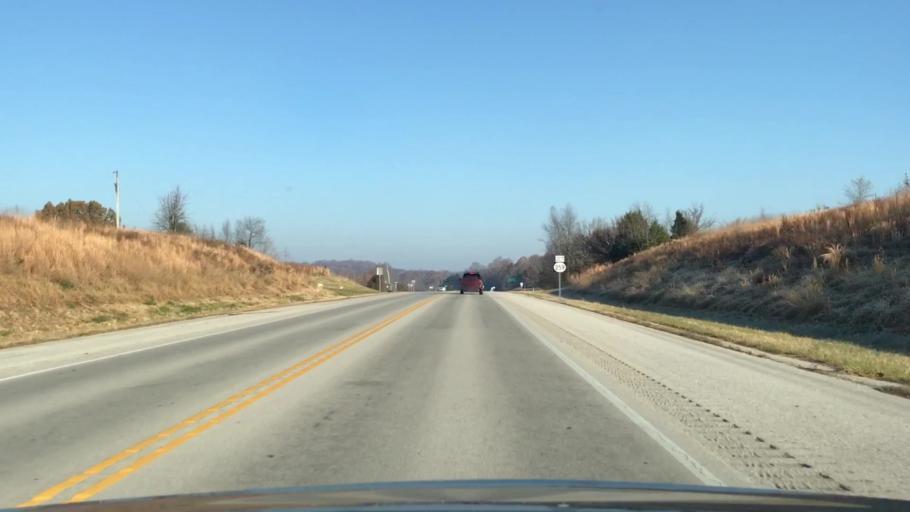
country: US
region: Kentucky
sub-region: Edmonson County
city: Brownsville
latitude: 37.1538
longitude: -86.2214
